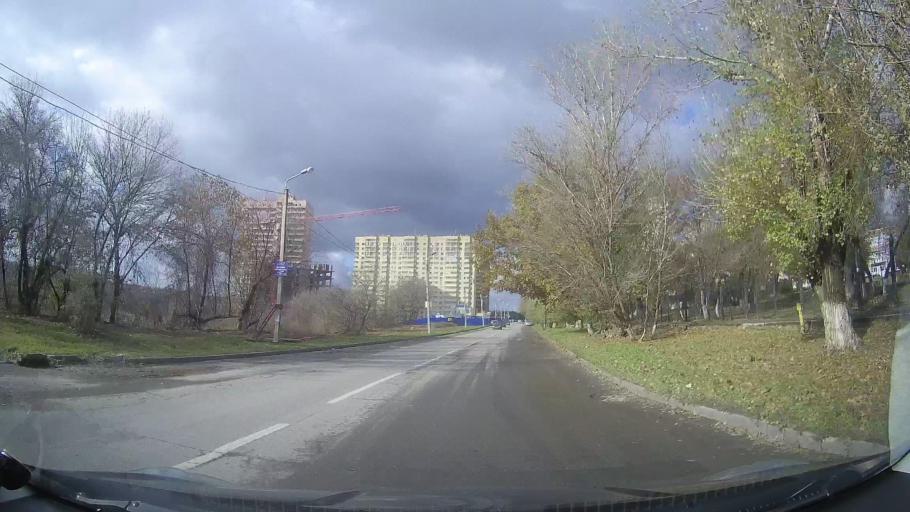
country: RU
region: Rostov
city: Severnyy
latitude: 47.2894
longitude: 39.6902
